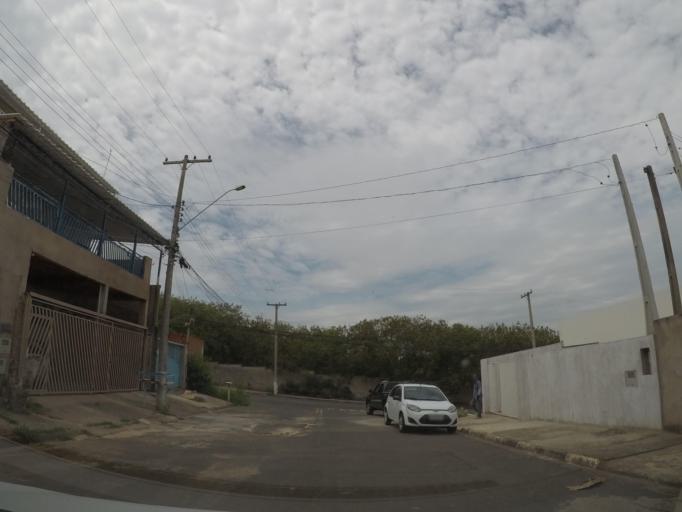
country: BR
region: Sao Paulo
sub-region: Hortolandia
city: Hortolandia
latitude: -22.8353
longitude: -47.2025
